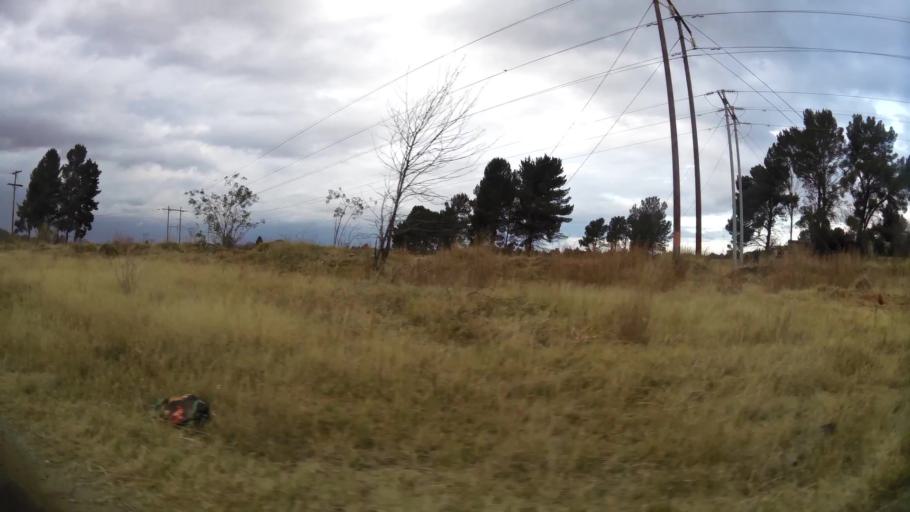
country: ZA
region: Orange Free State
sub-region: Lejweleputswa District Municipality
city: Welkom
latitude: -27.9617
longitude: 26.7151
